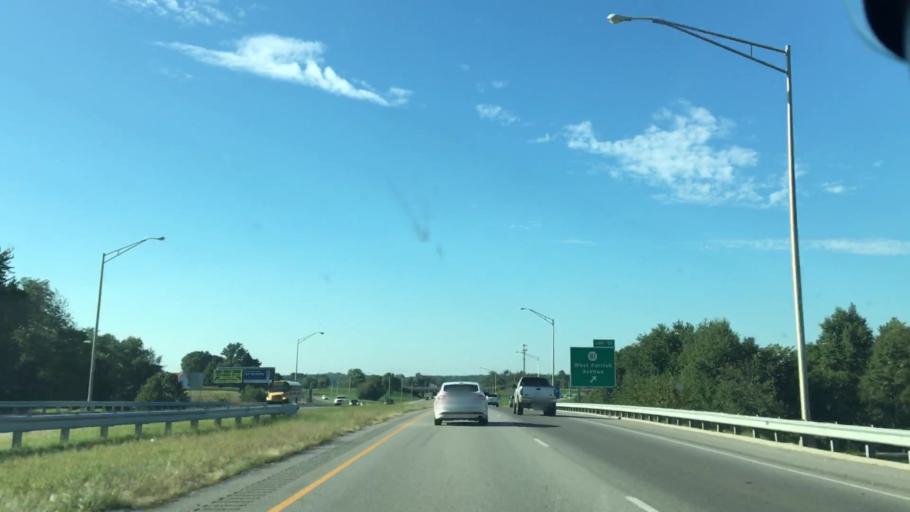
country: US
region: Kentucky
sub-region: Daviess County
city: Owensboro
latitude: 37.7505
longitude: -87.1564
